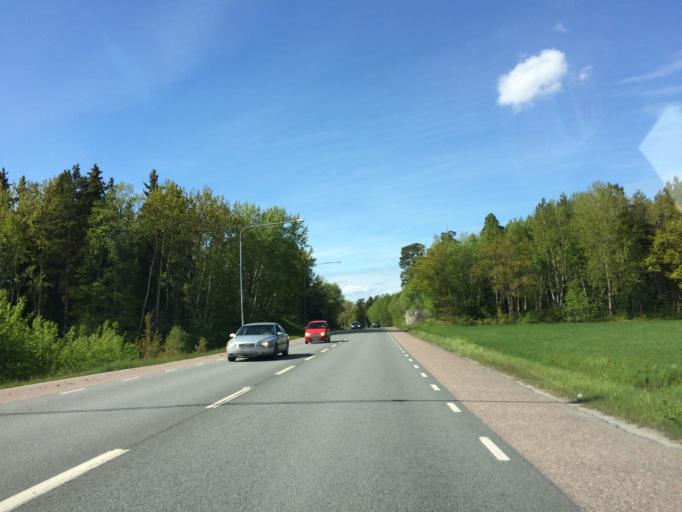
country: SE
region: Stockholm
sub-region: Norrtalje Kommun
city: Bergshamra
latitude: 59.4212
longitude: 18.0041
